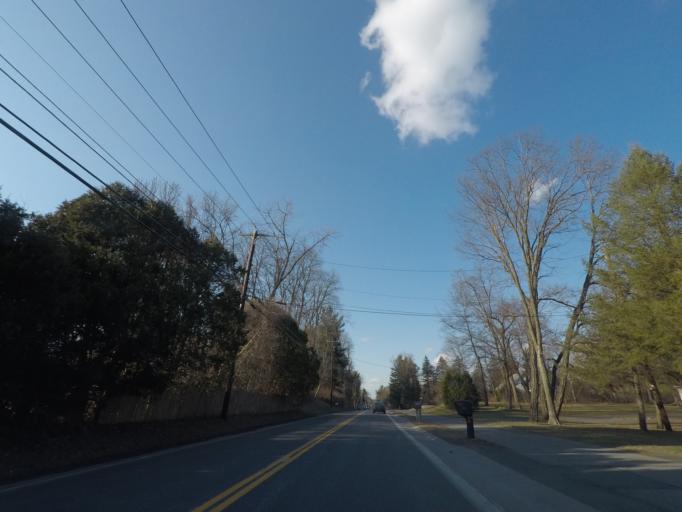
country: US
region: New York
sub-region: Saratoga County
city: Country Knolls
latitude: 42.8478
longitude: -73.7942
